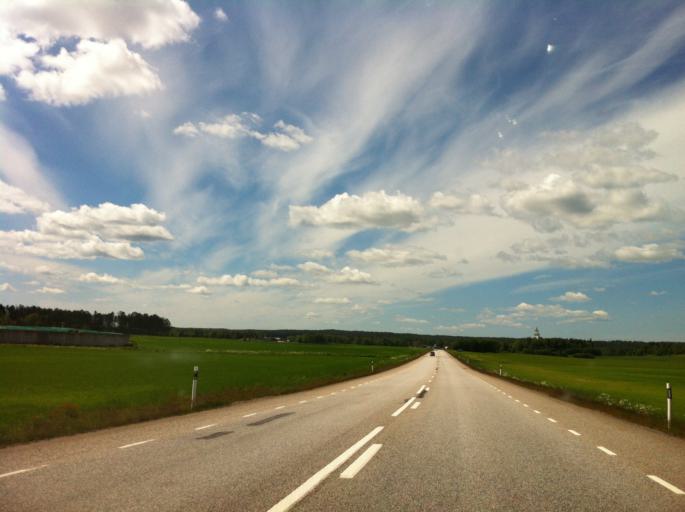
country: SE
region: Vaestra Goetaland
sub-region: Amals Kommun
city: Amal
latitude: 58.9823
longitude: 12.6512
